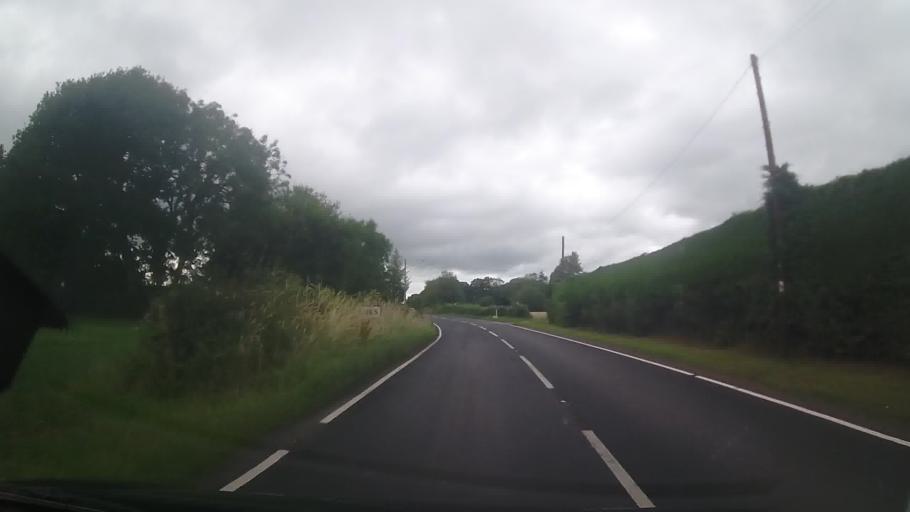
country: GB
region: England
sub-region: Cheshire West and Chester
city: Malpas
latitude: 52.9454
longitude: -2.7667
